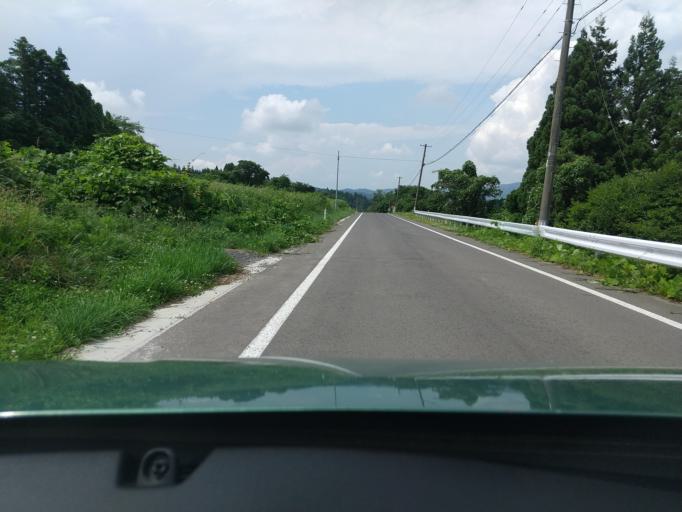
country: JP
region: Iwate
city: Ichinoseki
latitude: 38.9995
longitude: 141.2184
